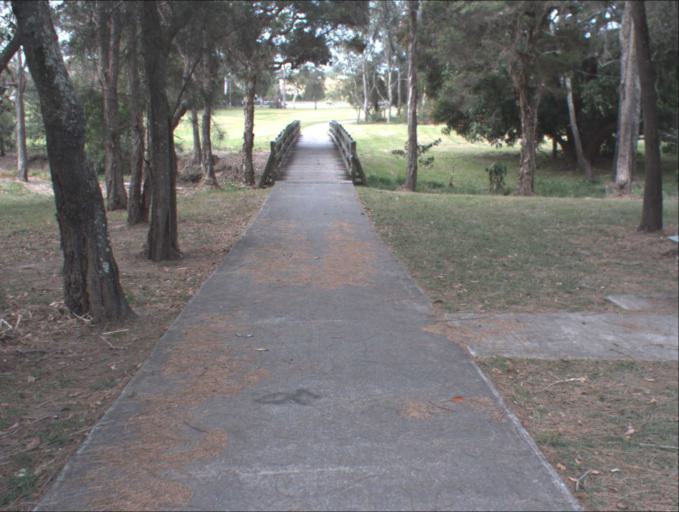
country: AU
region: Queensland
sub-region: Logan
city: Springwood
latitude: -27.6291
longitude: 153.1252
